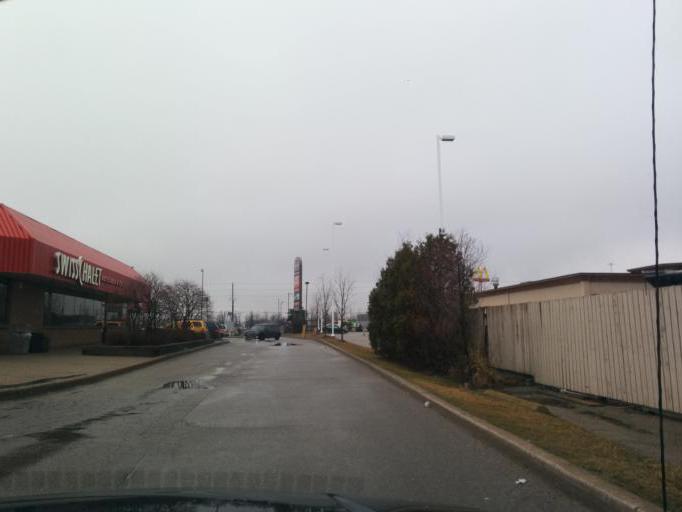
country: CA
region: Ontario
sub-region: Halton
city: Milton
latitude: 43.5225
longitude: -79.8995
